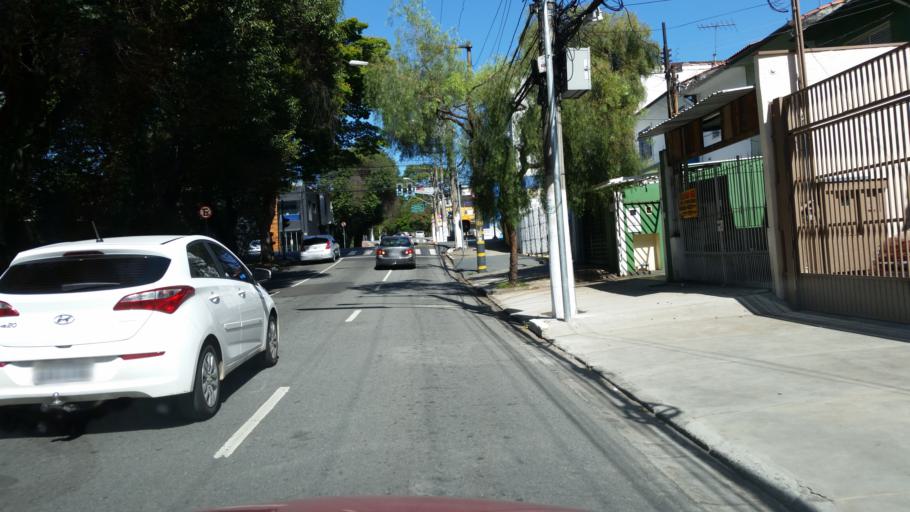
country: BR
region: Sao Paulo
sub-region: Diadema
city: Diadema
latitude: -23.6385
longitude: -46.6968
